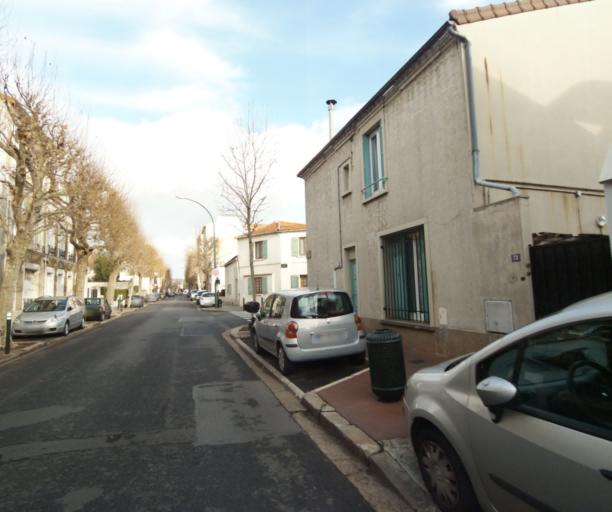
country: FR
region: Ile-de-France
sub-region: Departement des Hauts-de-Seine
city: La Garenne-Colombes
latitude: 48.9050
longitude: 2.2465
